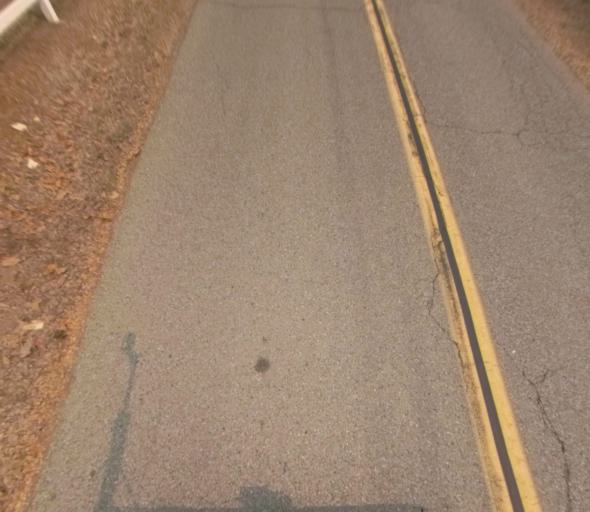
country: US
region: California
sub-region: Madera County
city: Oakhurst
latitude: 37.3429
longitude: -119.6130
